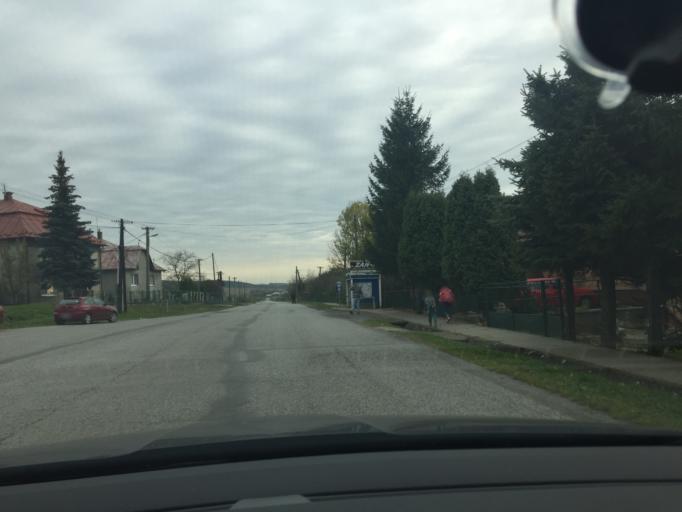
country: SK
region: Kosicky
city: Kosice
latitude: 48.8283
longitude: 21.3182
